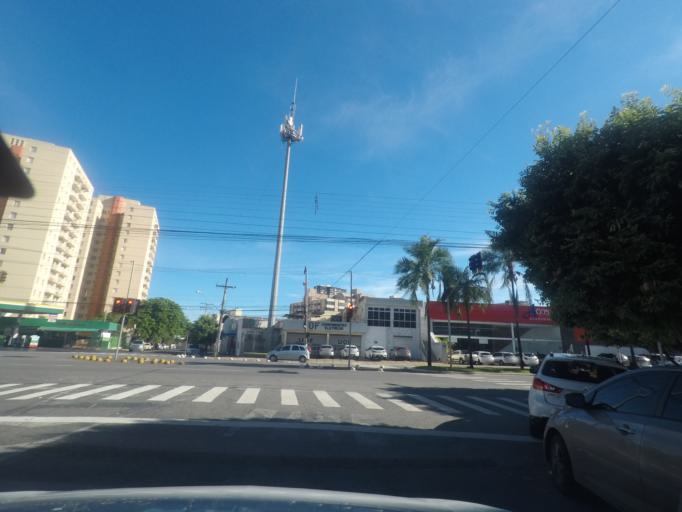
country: BR
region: Goias
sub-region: Goiania
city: Goiania
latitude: -16.6715
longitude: -49.2717
